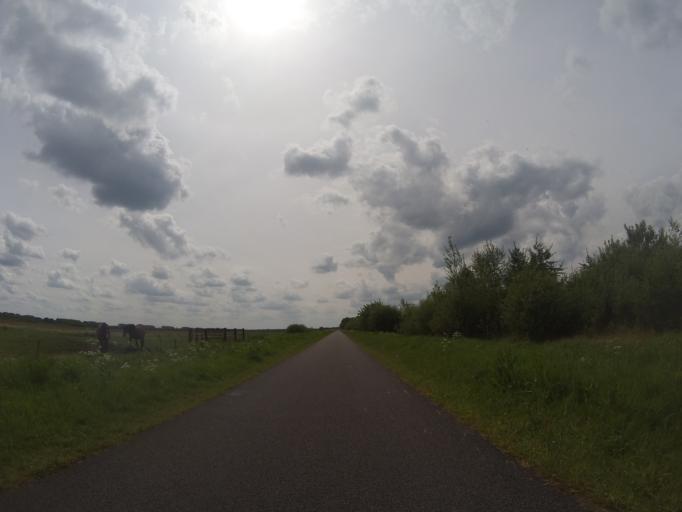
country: NL
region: Drenthe
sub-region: Gemeente Assen
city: Assen
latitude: 52.9017
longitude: 6.6311
